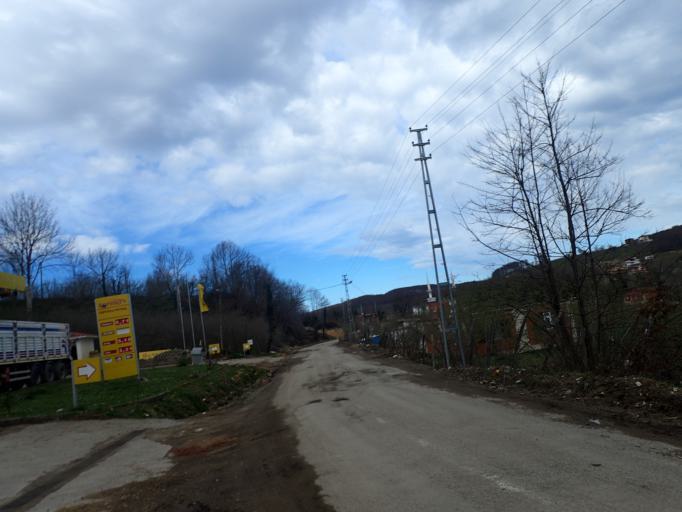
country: TR
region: Ordu
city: Kumru
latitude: 40.9397
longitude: 37.2611
